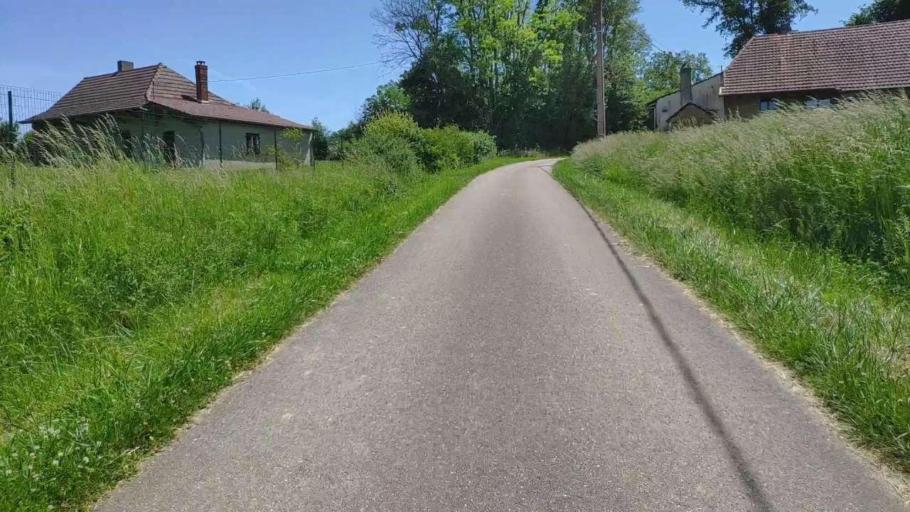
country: FR
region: Franche-Comte
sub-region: Departement du Jura
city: Bletterans
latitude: 46.7996
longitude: 5.3931
